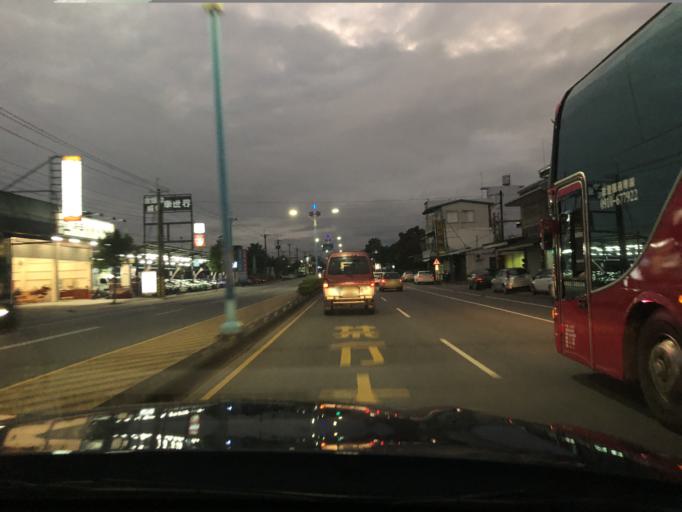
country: TW
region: Taiwan
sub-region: Hualien
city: Hualian
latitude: 23.9724
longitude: 121.5721
